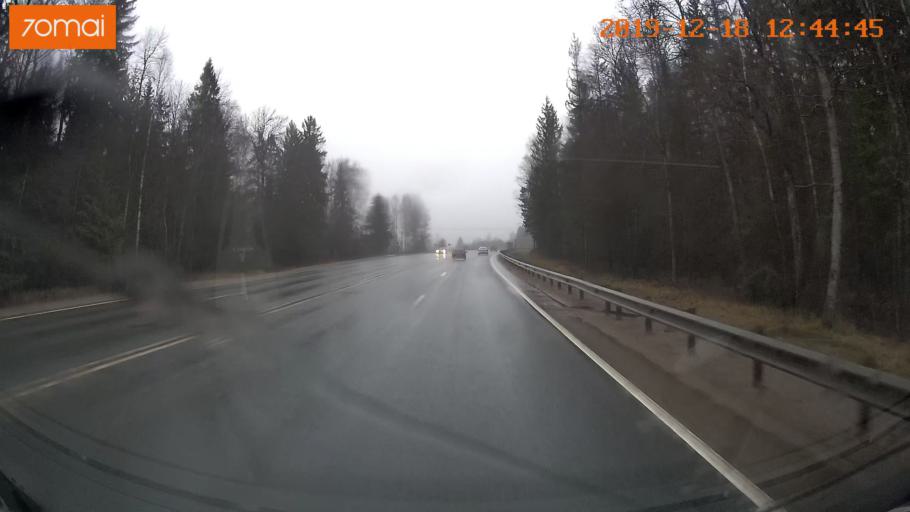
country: RU
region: Moskovskaya
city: Vysokovsk
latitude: 56.2236
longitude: 36.6504
